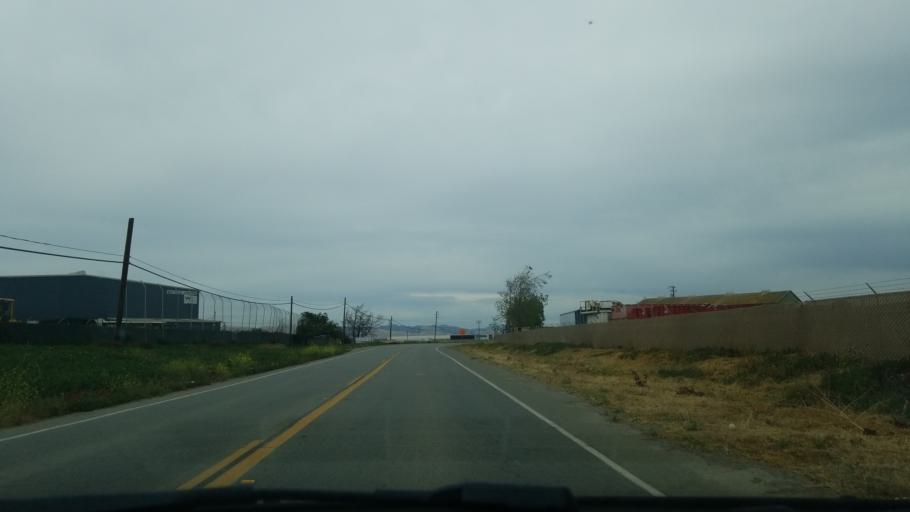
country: US
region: California
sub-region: Santa Barbara County
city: Santa Maria
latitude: 34.9186
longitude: -120.4785
